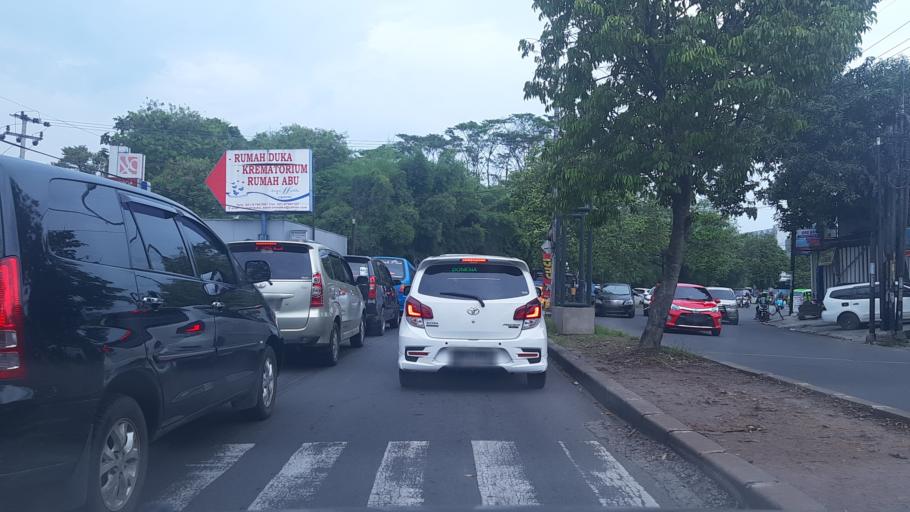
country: ID
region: West Java
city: Cibinong
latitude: -6.4804
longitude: 106.8647
